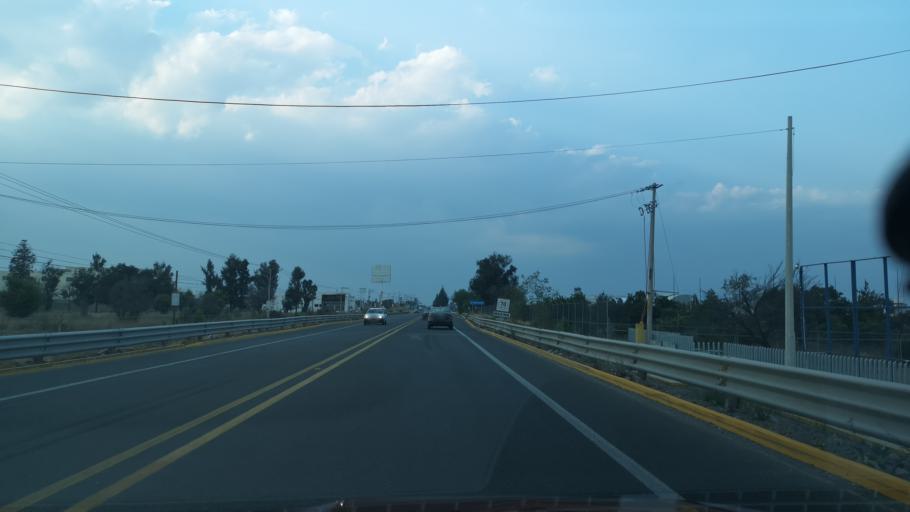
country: MX
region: Puebla
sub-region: Huejotzingo
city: Los Encinos
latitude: 19.1578
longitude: -98.3772
